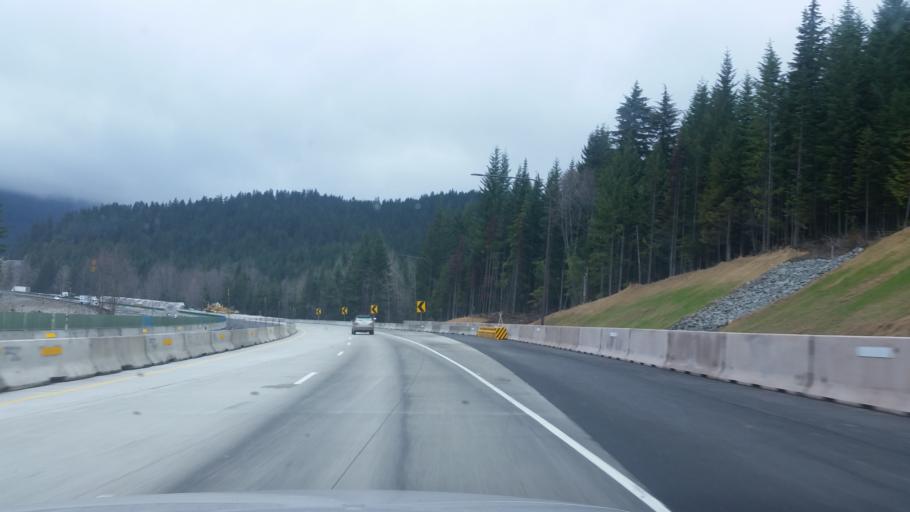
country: US
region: Washington
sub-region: King County
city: Tanner
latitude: 47.3385
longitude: -121.3496
